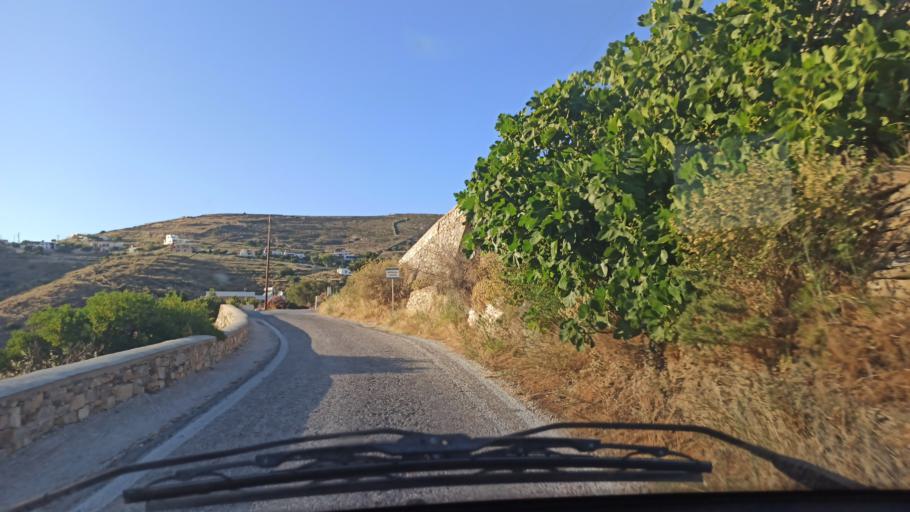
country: GR
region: South Aegean
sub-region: Nomos Kykladon
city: Ano Syros
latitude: 37.4592
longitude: 24.9316
